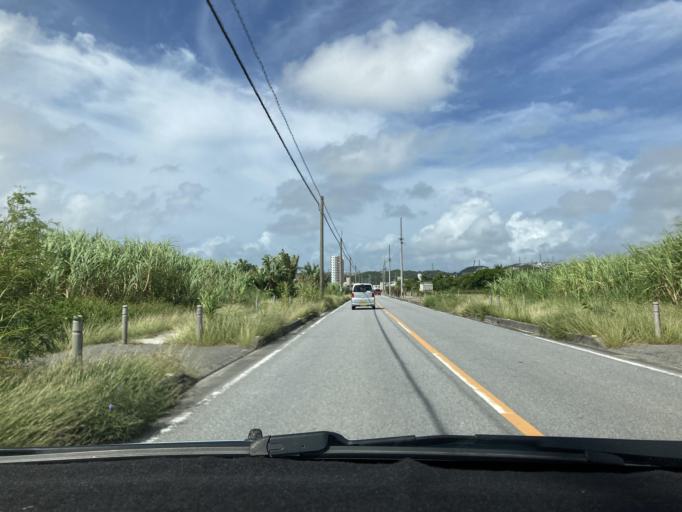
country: JP
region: Okinawa
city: Ginowan
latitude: 26.2220
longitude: 127.7726
